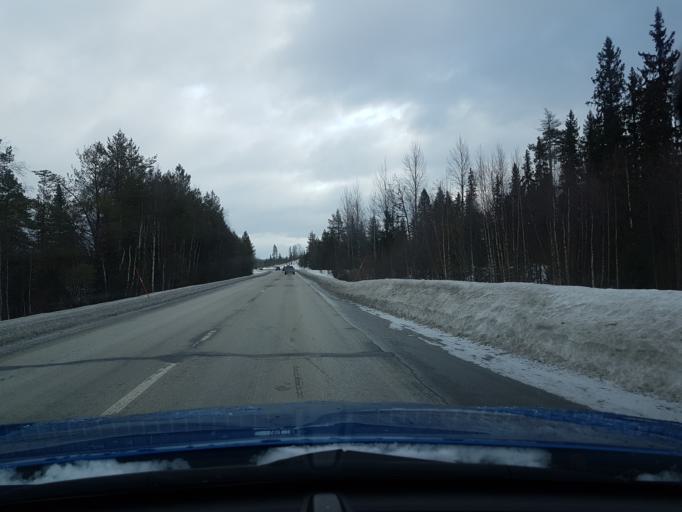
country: SE
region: Jaemtland
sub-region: Harjedalens Kommun
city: Sveg
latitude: 62.4112
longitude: 13.5785
